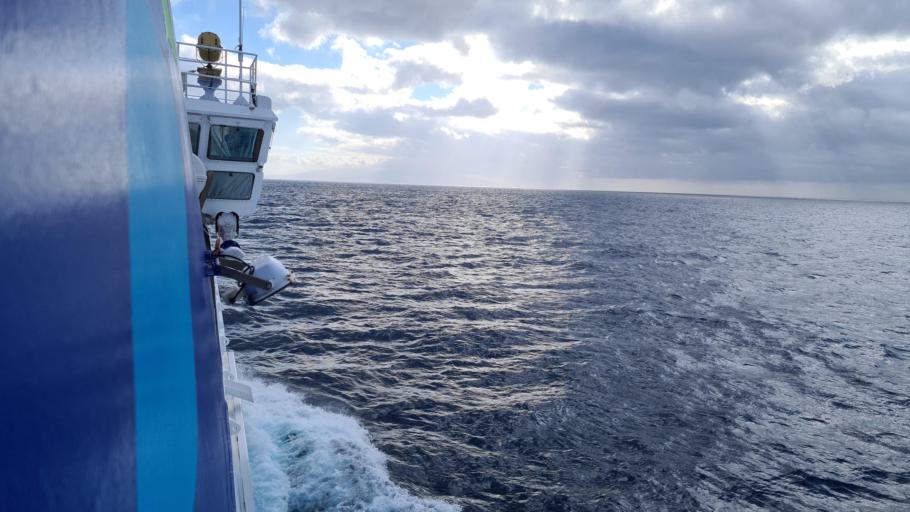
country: PT
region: Azores
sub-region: Sao Roque do Pico
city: Sao Roque do Pico
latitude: 38.6308
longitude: -28.3270
